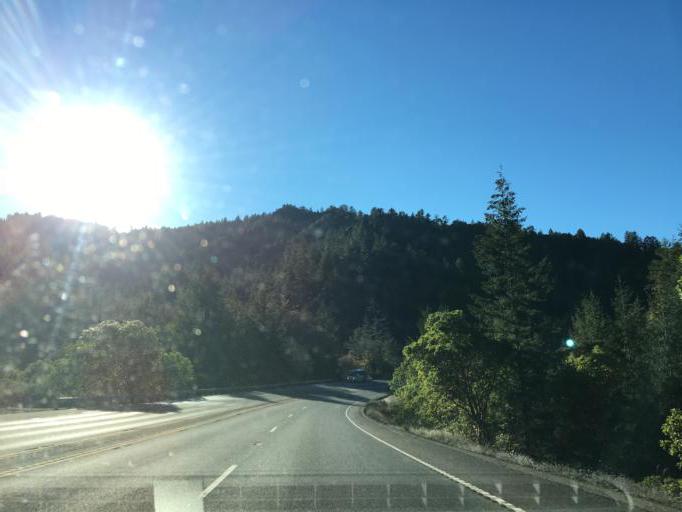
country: US
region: California
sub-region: Mendocino County
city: Laytonville
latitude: 39.8283
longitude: -123.6053
